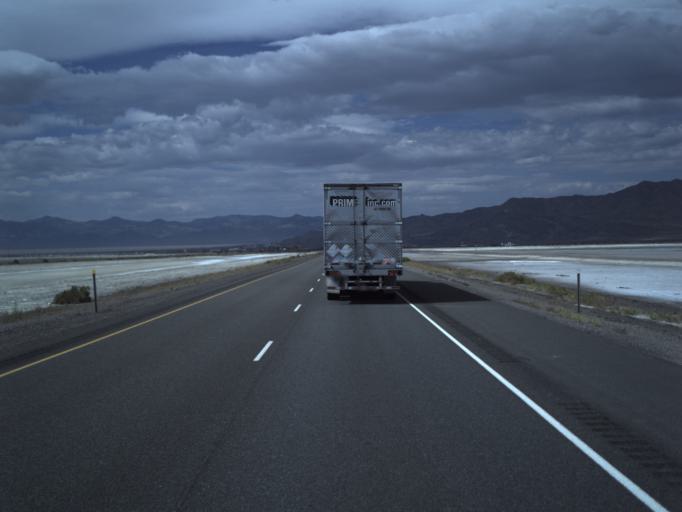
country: US
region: Utah
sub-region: Tooele County
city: Wendover
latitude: 40.7411
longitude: -113.9387
